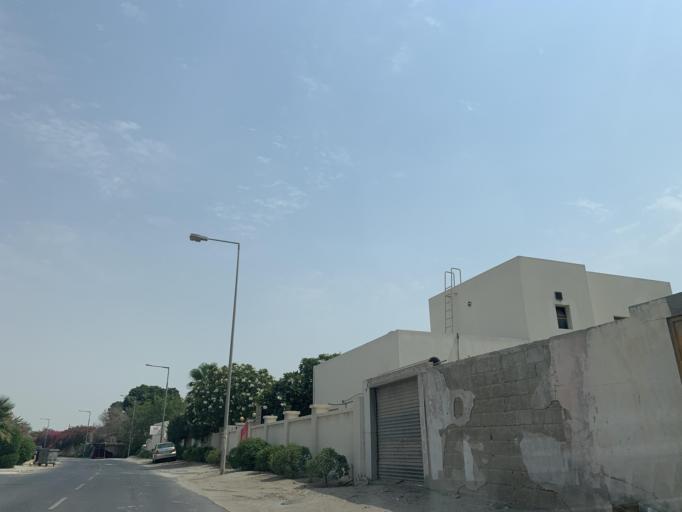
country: BH
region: Manama
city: Jidd Hafs
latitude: 26.2120
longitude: 50.4849
